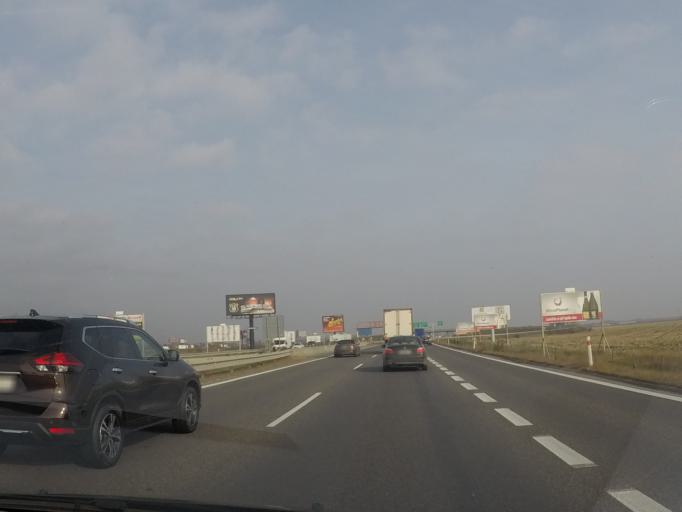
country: SK
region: Bratislavsky
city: Svaty Jur
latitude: 48.1825
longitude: 17.1966
